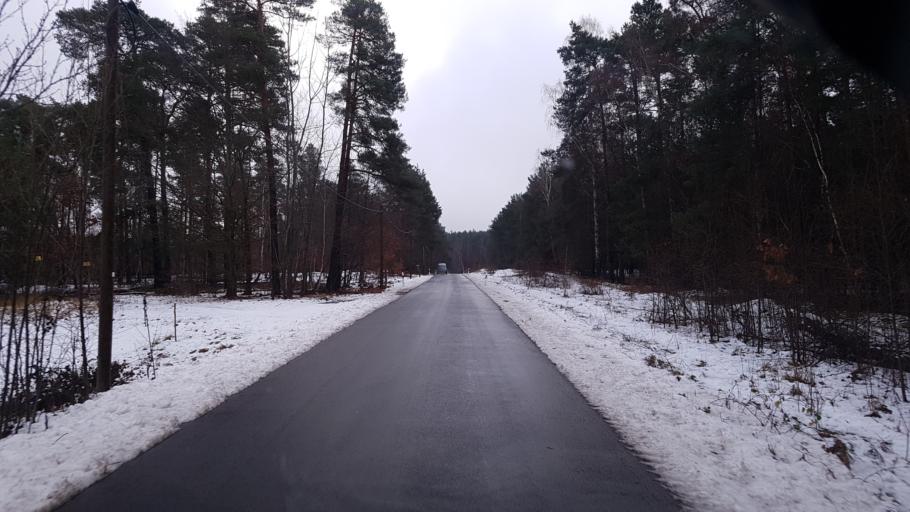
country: DE
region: Brandenburg
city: Straupitz
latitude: 51.9742
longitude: 14.1989
